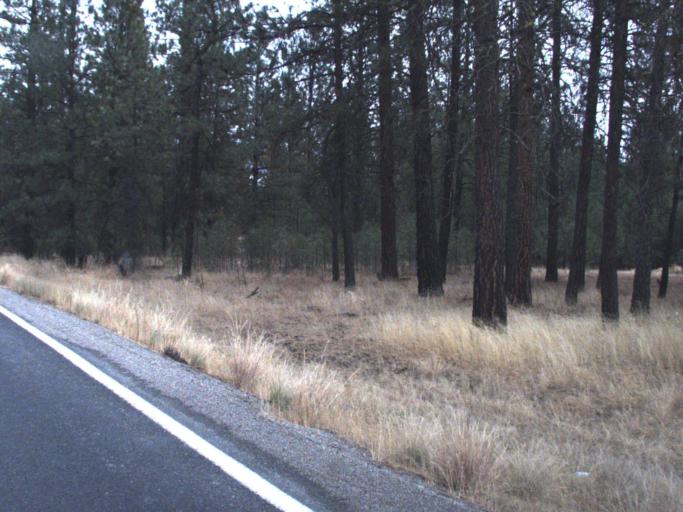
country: US
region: Washington
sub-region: Spokane County
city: Fairchild Air Force Base
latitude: 47.8531
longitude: -117.8485
